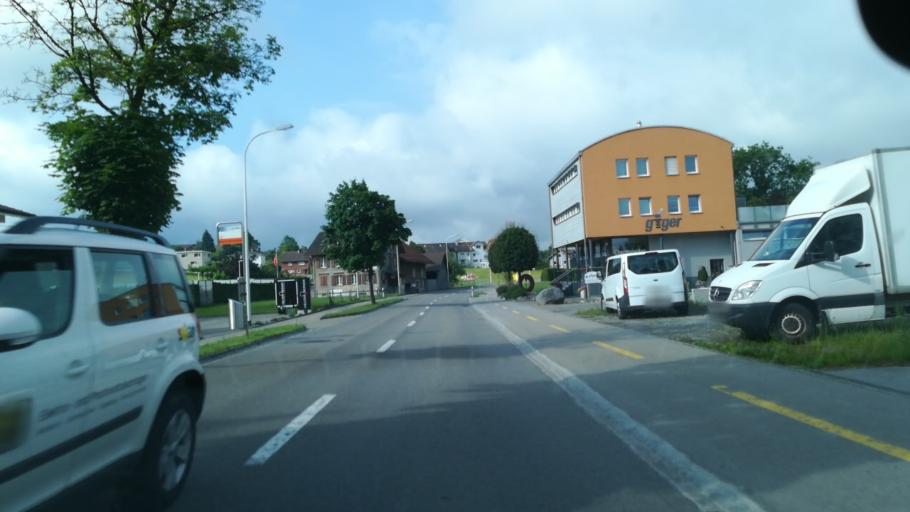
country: CH
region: Saint Gallen
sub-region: Wahlkreis St. Gallen
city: Andwil
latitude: 47.4392
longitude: 9.2544
